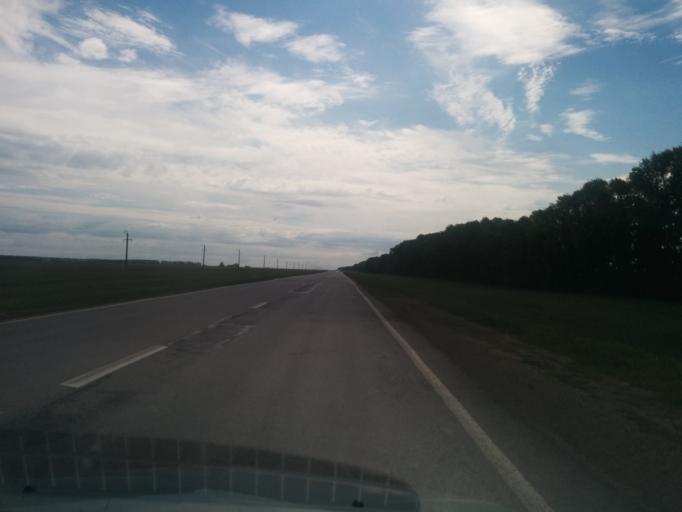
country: RU
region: Bashkortostan
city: Karmaskaly
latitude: 54.4189
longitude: 56.0481
